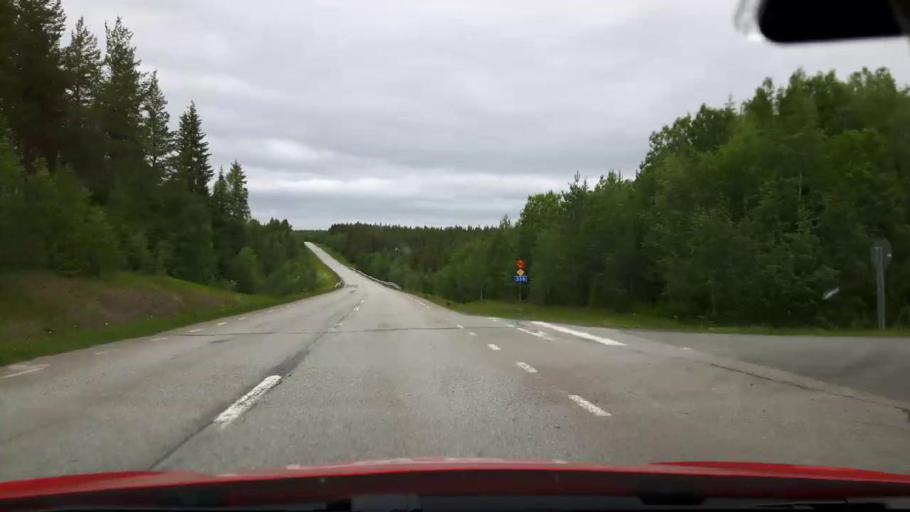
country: SE
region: Jaemtland
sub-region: OEstersunds Kommun
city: Lit
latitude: 63.6112
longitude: 14.6746
